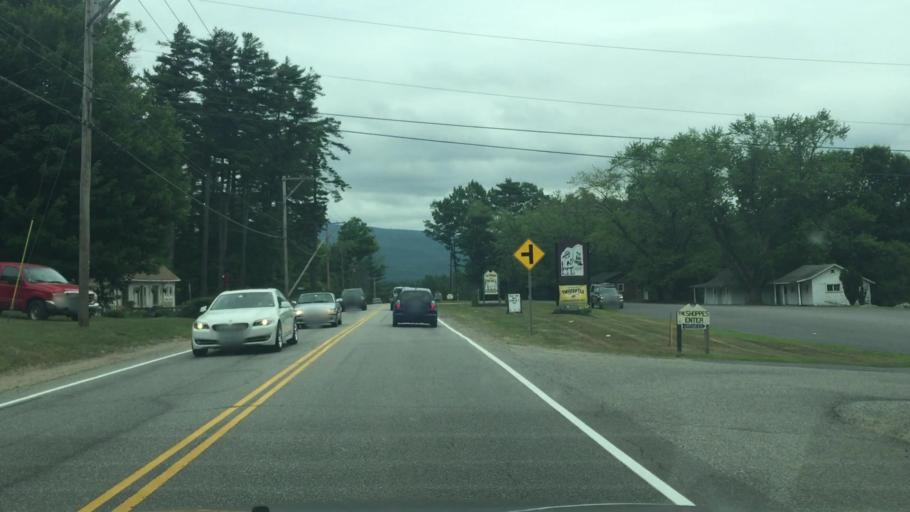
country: US
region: New Hampshire
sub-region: Carroll County
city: Moultonborough
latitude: 43.7295
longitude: -71.4232
